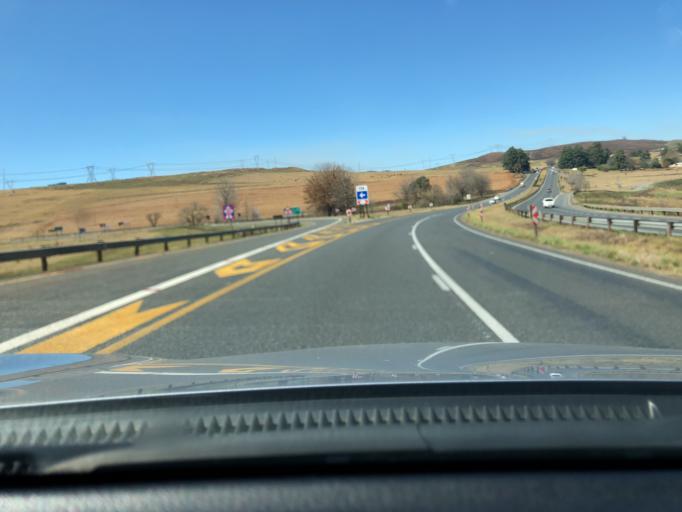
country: ZA
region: KwaZulu-Natal
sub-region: uMgungundlovu District Municipality
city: Howick
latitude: -29.4175
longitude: 30.1636
